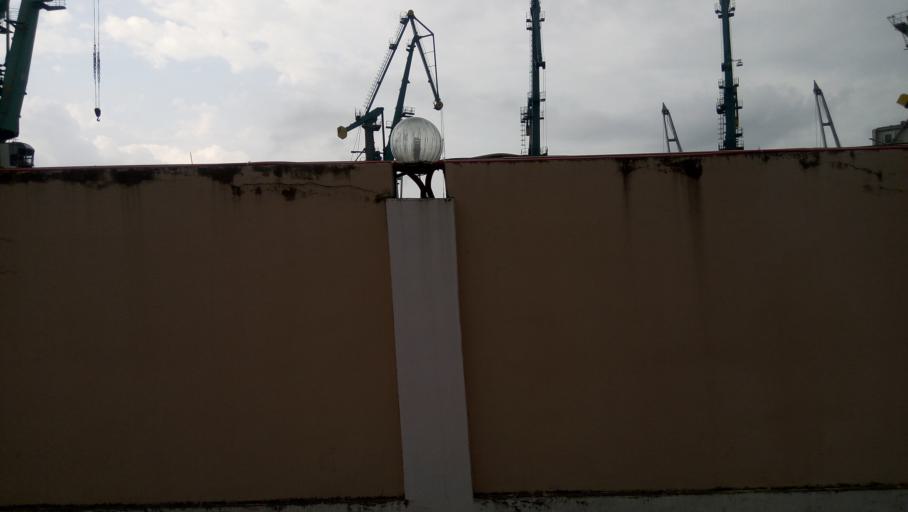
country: GE
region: Ajaria
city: Batumi
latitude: 41.6462
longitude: 41.6527
